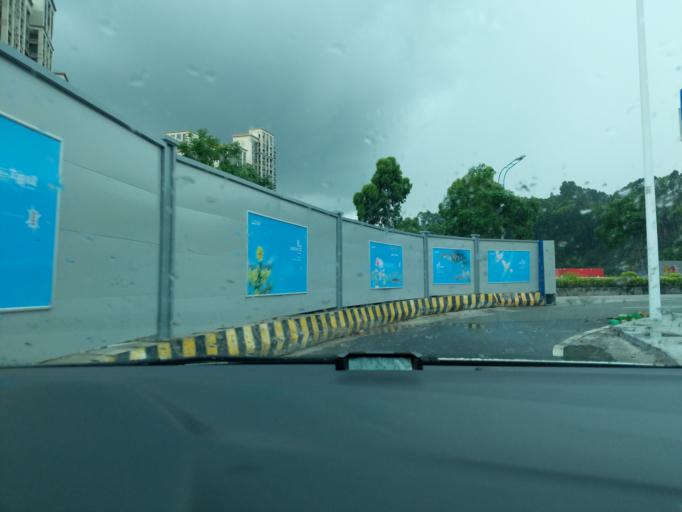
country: CN
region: Guangdong
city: Huangge
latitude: 22.7966
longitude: 113.5158
